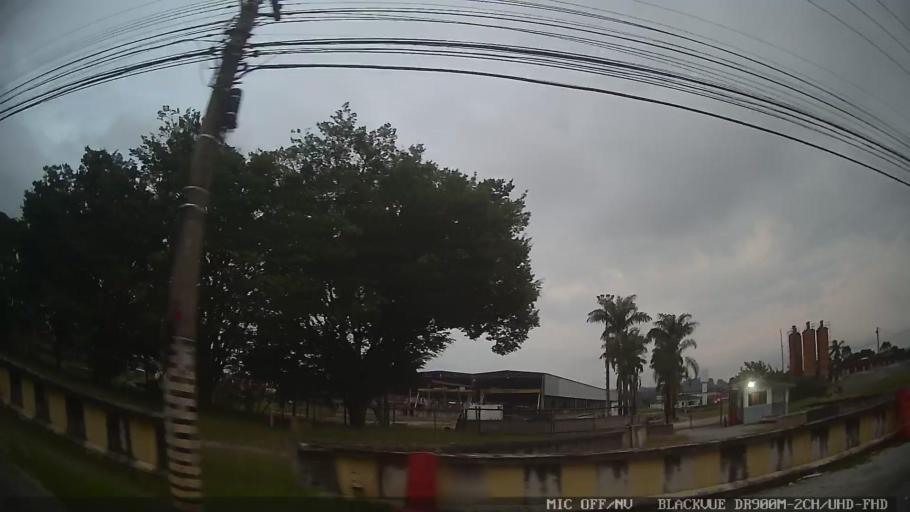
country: BR
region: Sao Paulo
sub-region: Suzano
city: Suzano
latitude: -23.5359
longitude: -46.2989
